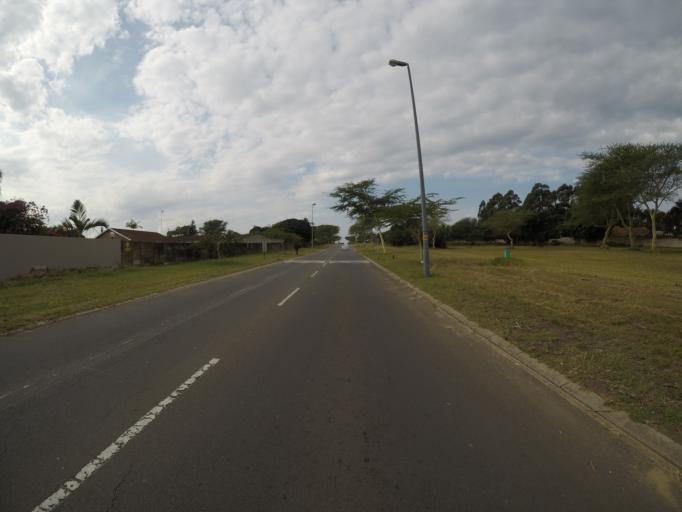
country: ZA
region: KwaZulu-Natal
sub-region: uThungulu District Municipality
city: Richards Bay
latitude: -28.7385
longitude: 32.0788
